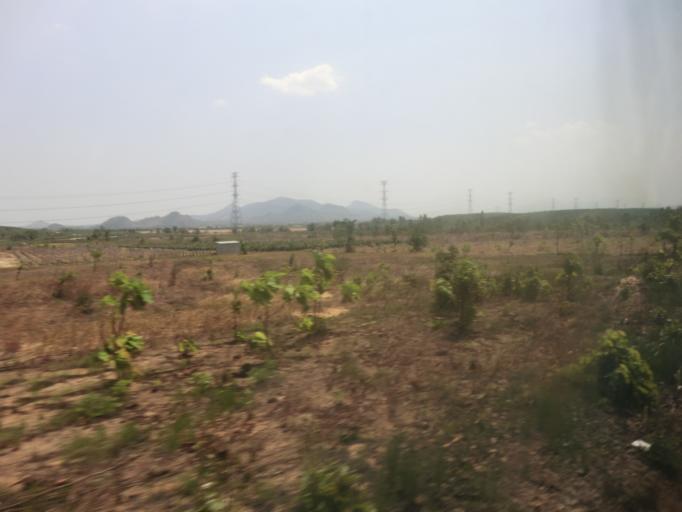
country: VN
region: Binh Thuan
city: Thuan Nam
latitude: 10.8786
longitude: 107.8055
